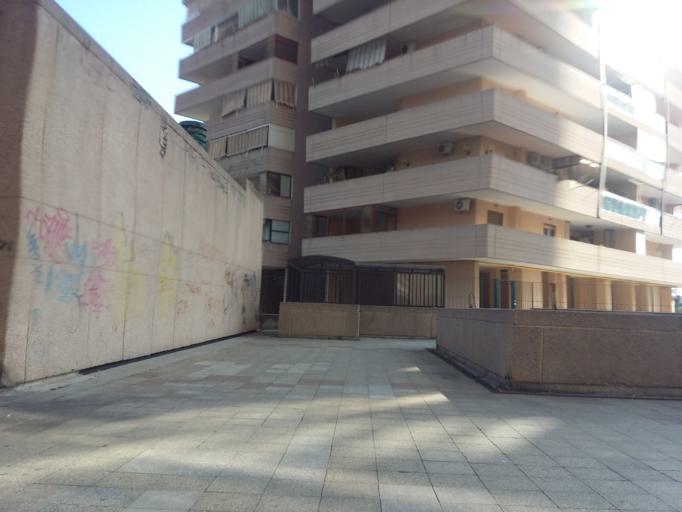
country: IT
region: Campania
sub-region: Provincia di Napoli
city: Napoli
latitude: 40.8558
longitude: 14.2803
